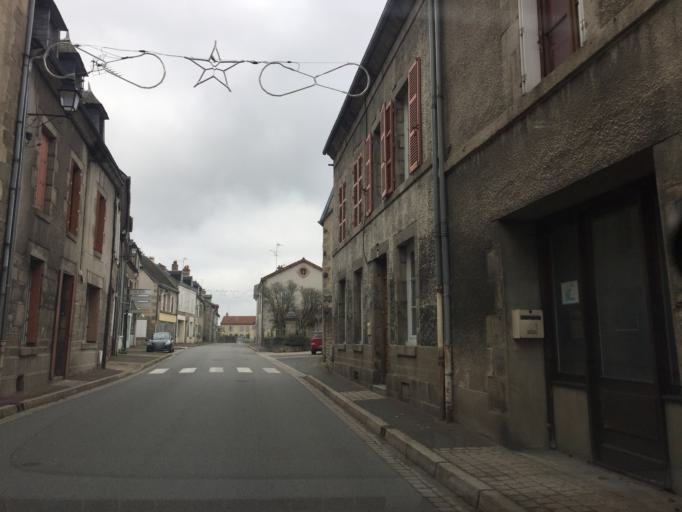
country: FR
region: Limousin
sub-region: Departement de la Creuse
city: Ahun
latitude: 46.0870
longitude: 2.0451
